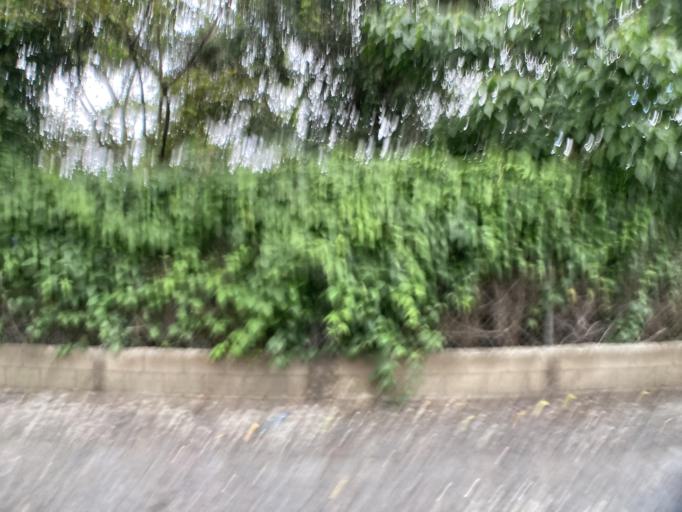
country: GT
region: Sacatepequez
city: Antigua Guatemala
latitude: 14.5682
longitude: -90.7418
